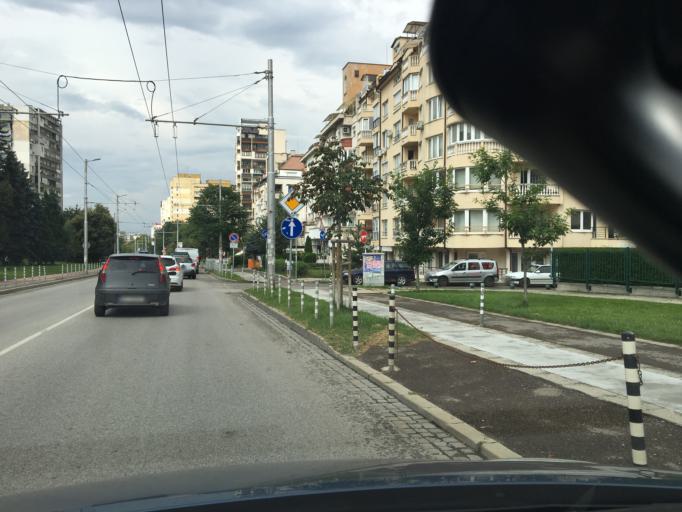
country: BG
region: Sofia-Capital
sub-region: Stolichna Obshtina
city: Sofia
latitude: 42.6668
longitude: 23.2760
